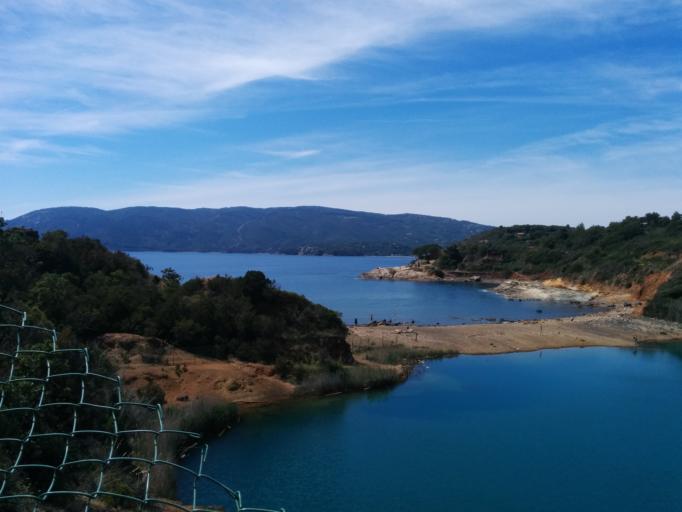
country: IT
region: Tuscany
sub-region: Provincia di Livorno
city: Porto Azzurro
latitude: 42.7747
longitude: 10.4208
